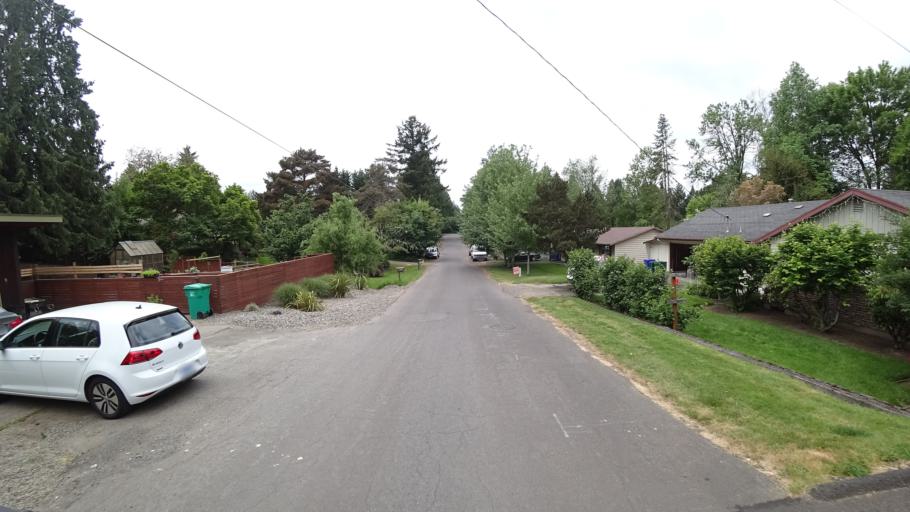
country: US
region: Oregon
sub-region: Washington County
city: Garden Home-Whitford
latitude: 45.4739
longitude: -122.7370
